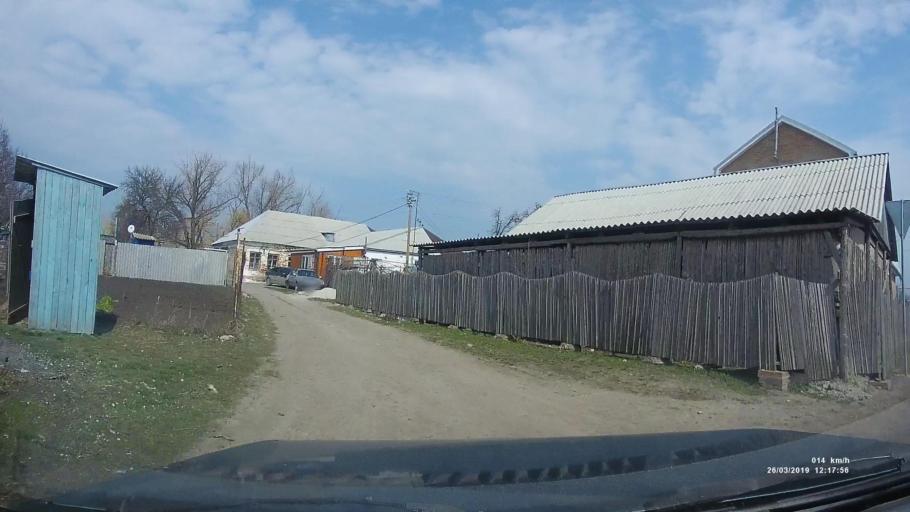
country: RU
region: Rostov
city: Novobessergenovka
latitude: 47.1461
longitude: 38.6426
